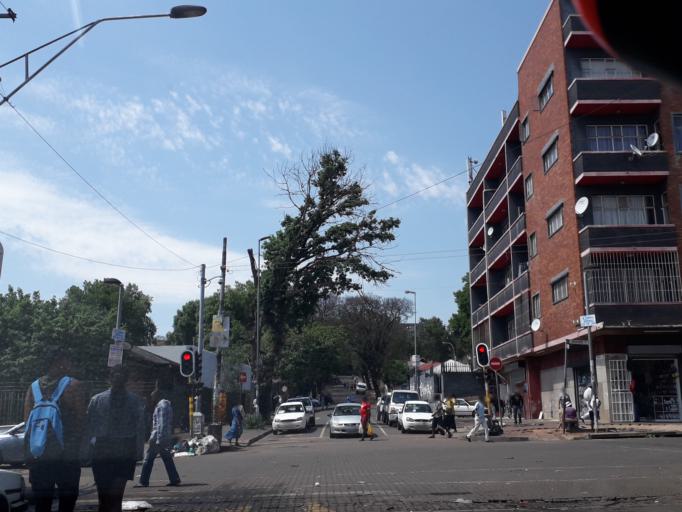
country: ZA
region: Gauteng
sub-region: City of Johannesburg Metropolitan Municipality
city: Johannesburg
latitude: -26.1811
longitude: 28.0648
